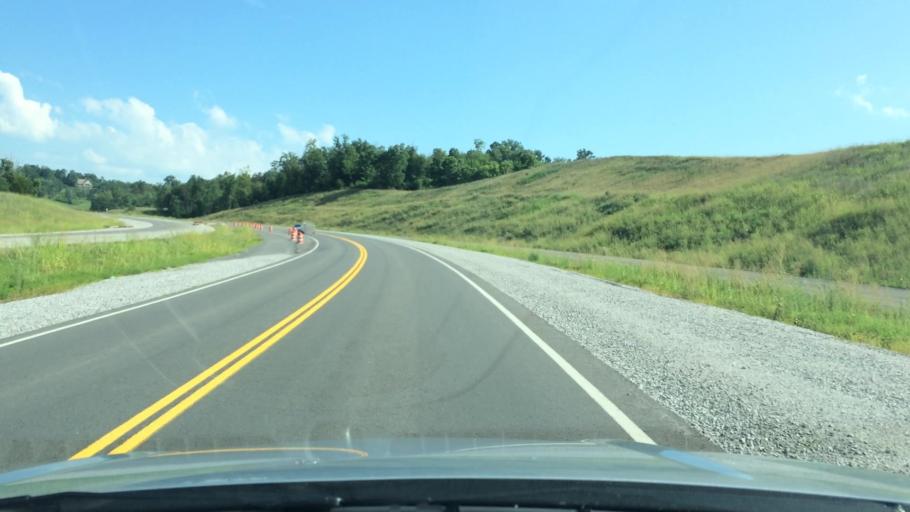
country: US
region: Tennessee
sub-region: Jefferson County
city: White Pine
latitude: 36.1260
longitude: -83.3336
